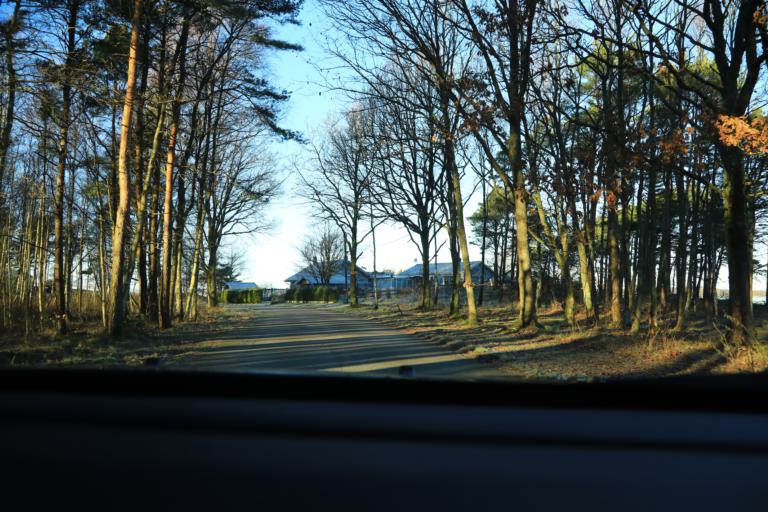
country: SE
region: Halland
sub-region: Varbergs Kommun
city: Varberg
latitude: 57.2019
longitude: 12.1883
